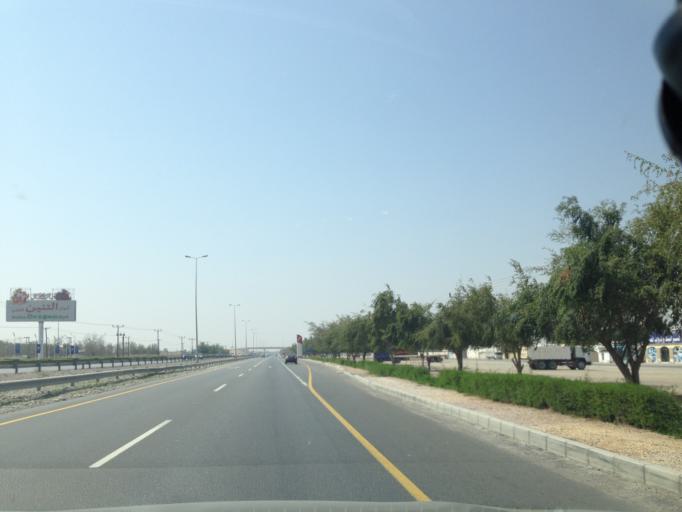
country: OM
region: Al Batinah
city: Barka'
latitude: 23.6654
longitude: 57.9560
